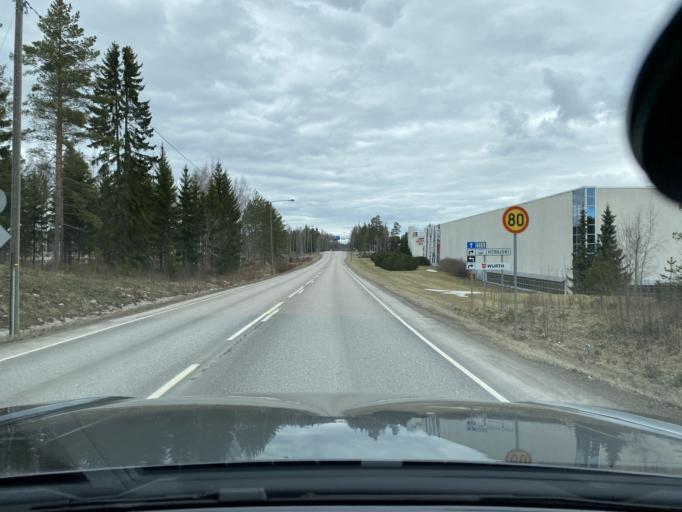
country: FI
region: Haeme
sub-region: Riihimaeki
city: Riihimaeki
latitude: 60.6908
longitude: 24.7494
